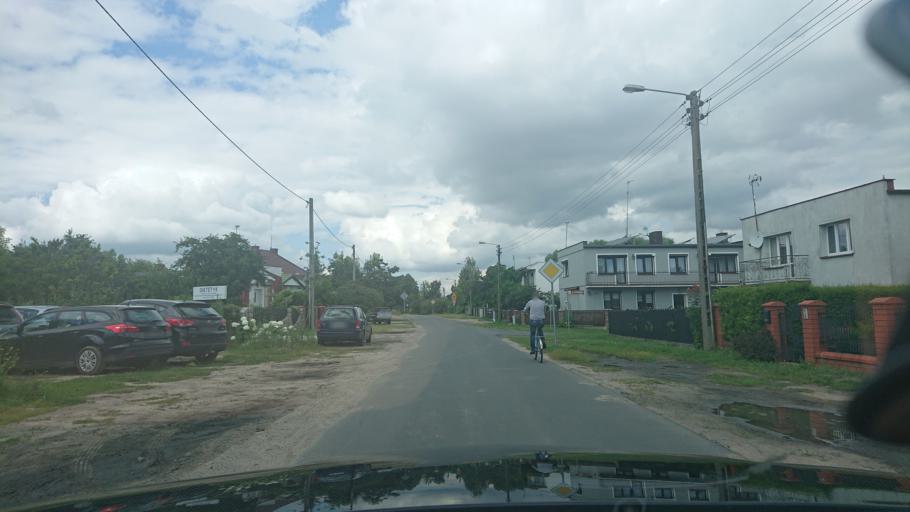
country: PL
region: Greater Poland Voivodeship
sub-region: Powiat gnieznienski
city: Gniezno
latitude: 52.5139
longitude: 17.6195
